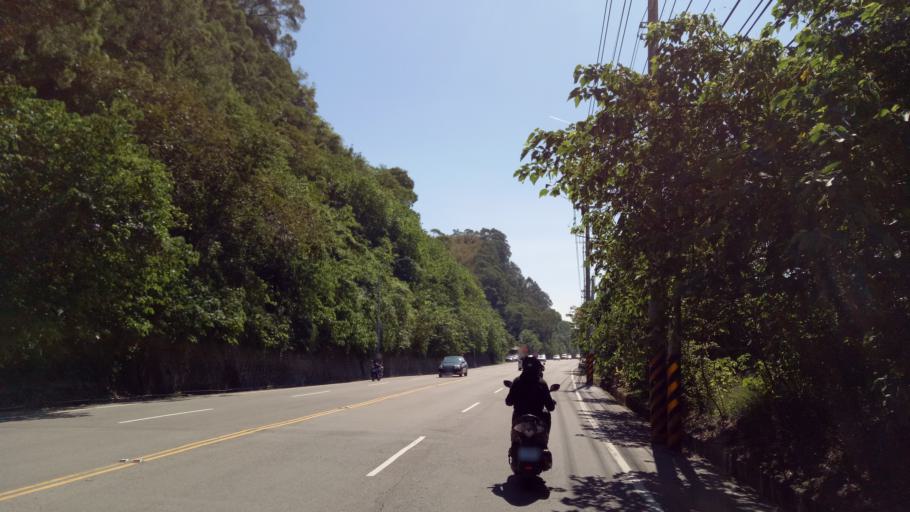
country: TW
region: Taiwan
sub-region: Hsinchu
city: Hsinchu
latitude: 24.6781
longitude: 120.9660
